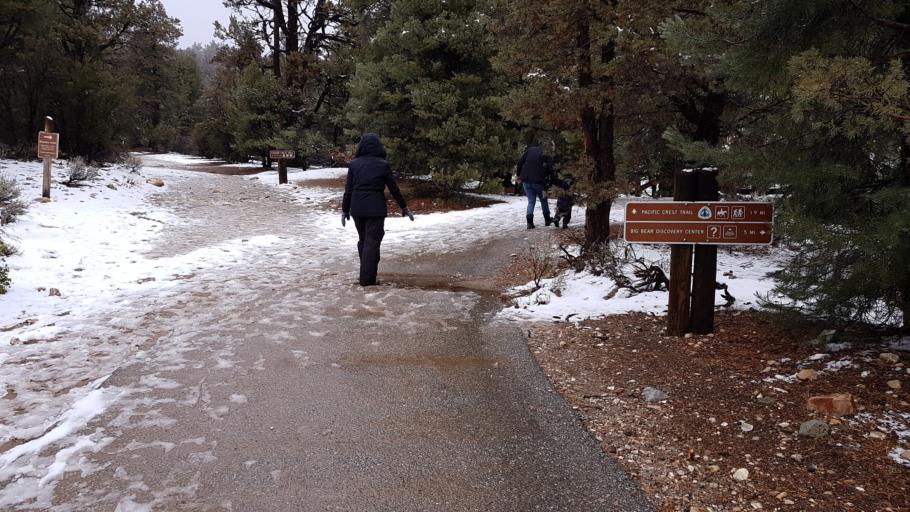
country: US
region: California
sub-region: San Bernardino County
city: Big Bear Lake
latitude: 34.2649
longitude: -116.9108
